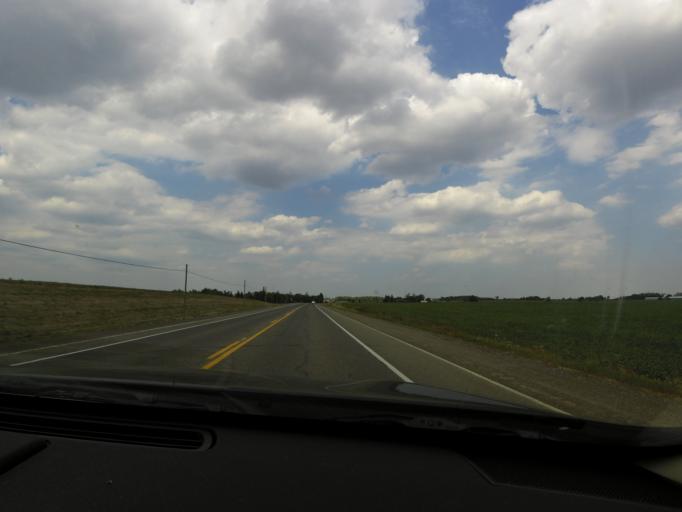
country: CA
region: Ontario
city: Brampton
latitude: 43.7462
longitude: -79.9083
